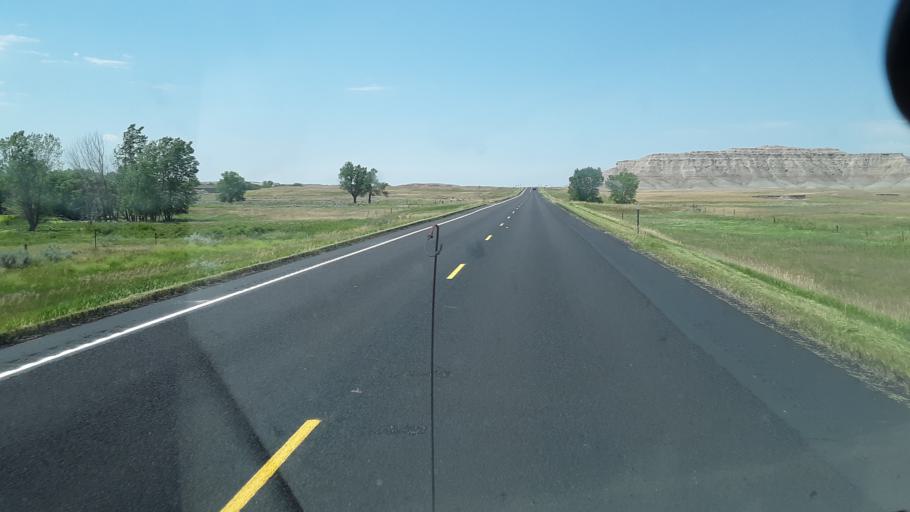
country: US
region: South Dakota
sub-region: Haakon County
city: Philip
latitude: 43.7193
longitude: -102.0113
